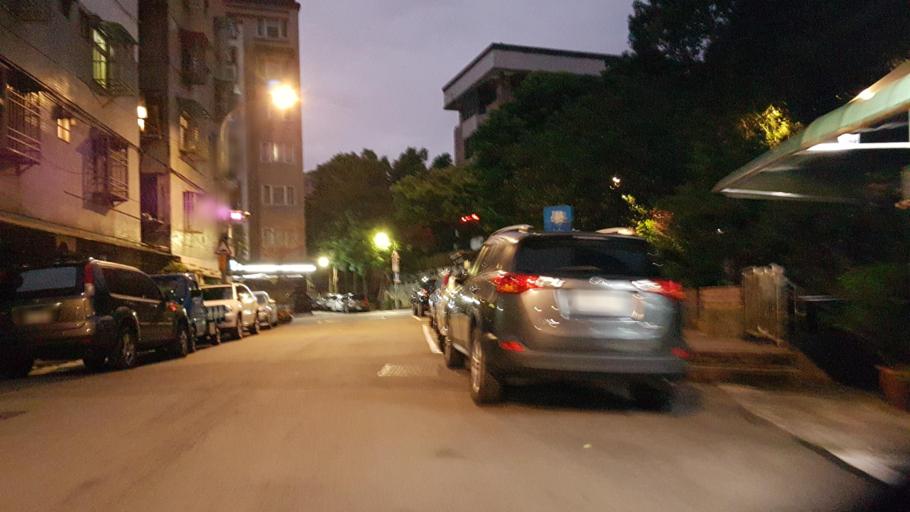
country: TW
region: Taipei
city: Taipei
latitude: 24.9958
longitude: 121.5478
